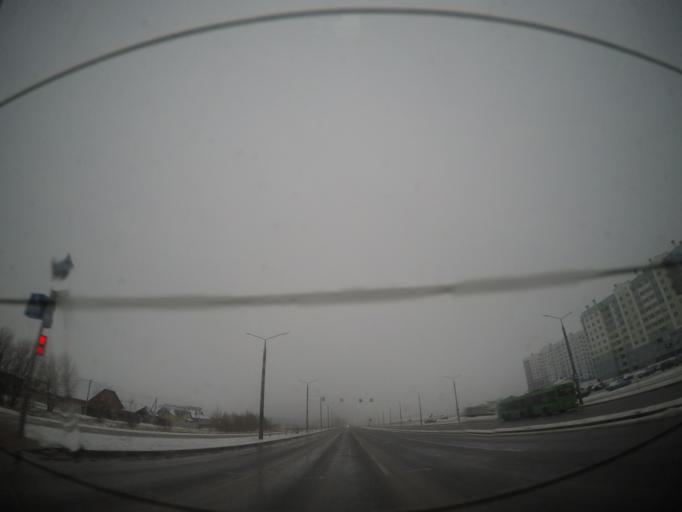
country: BY
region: Grodnenskaya
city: Hrodna
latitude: 53.6146
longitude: 23.8214
